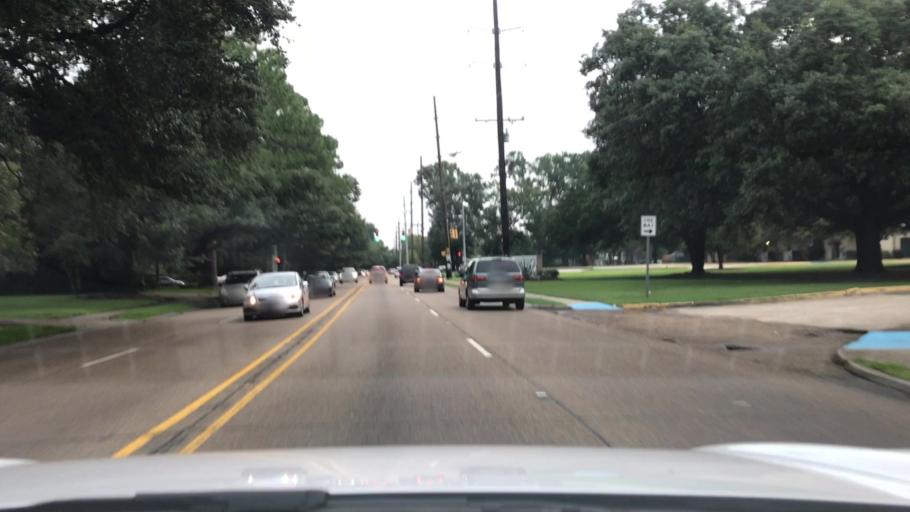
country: US
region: Louisiana
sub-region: East Baton Rouge Parish
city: Baton Rouge
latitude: 30.4301
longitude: -91.1354
